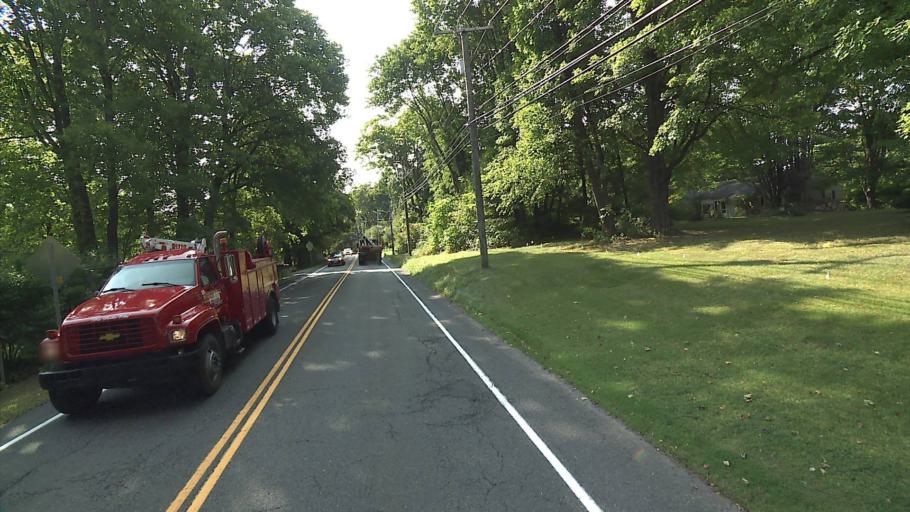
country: US
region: Connecticut
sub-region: Fairfield County
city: Bethel
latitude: 41.3132
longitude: -73.3502
